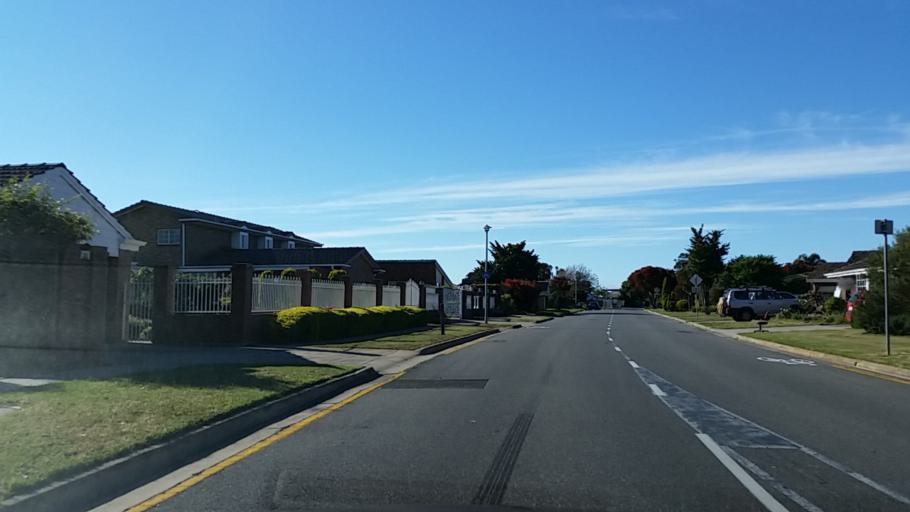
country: AU
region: South Australia
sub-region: Charles Sturt
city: West Lakes Shore
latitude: -34.8720
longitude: 138.4941
